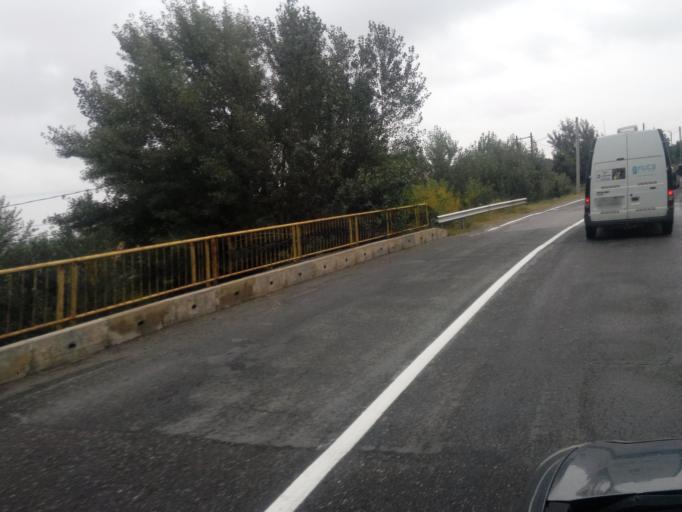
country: RO
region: Cluj
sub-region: Comuna Moldovenesti
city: Moldovenesti
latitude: 46.5114
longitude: 23.6620
